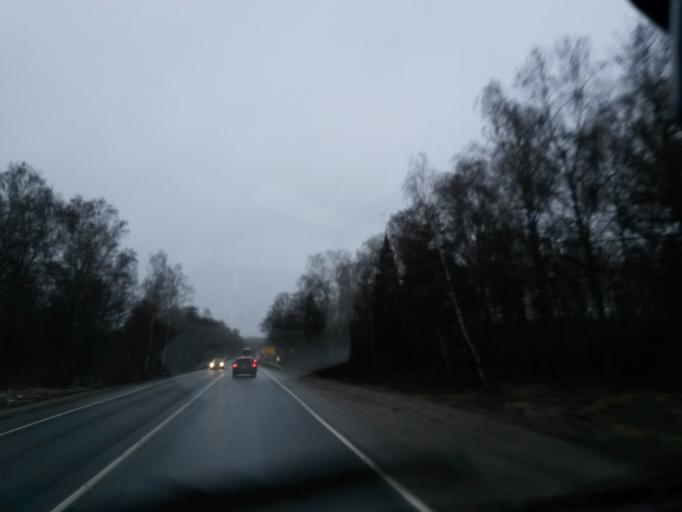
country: RU
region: Moskovskaya
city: Dubrovitsy
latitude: 55.3747
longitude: 37.4039
